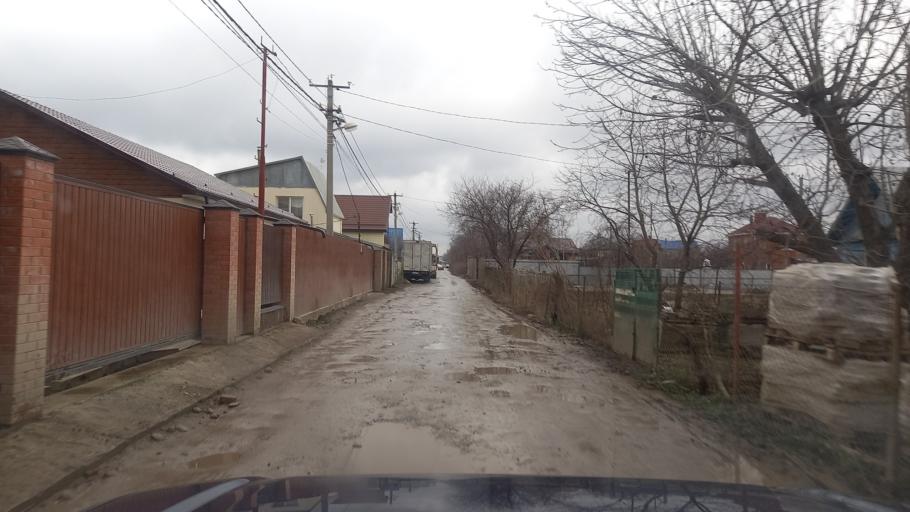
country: RU
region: Krasnodarskiy
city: Pashkovskiy
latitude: 45.0566
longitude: 39.1738
